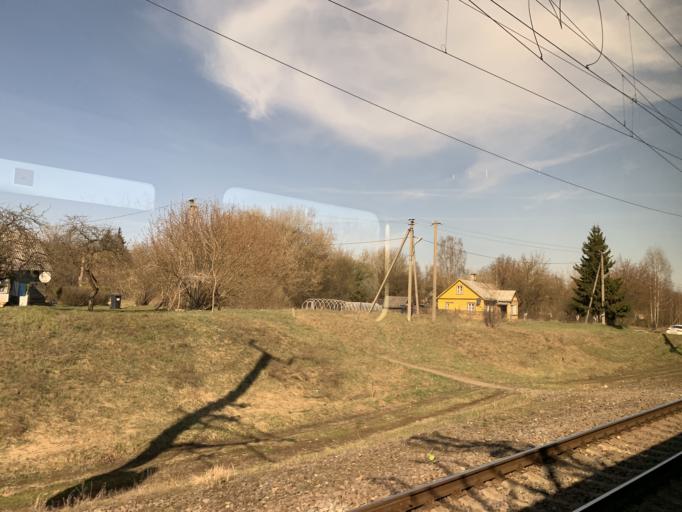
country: LT
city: Skaidiskes
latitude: 54.6966
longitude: 25.4335
